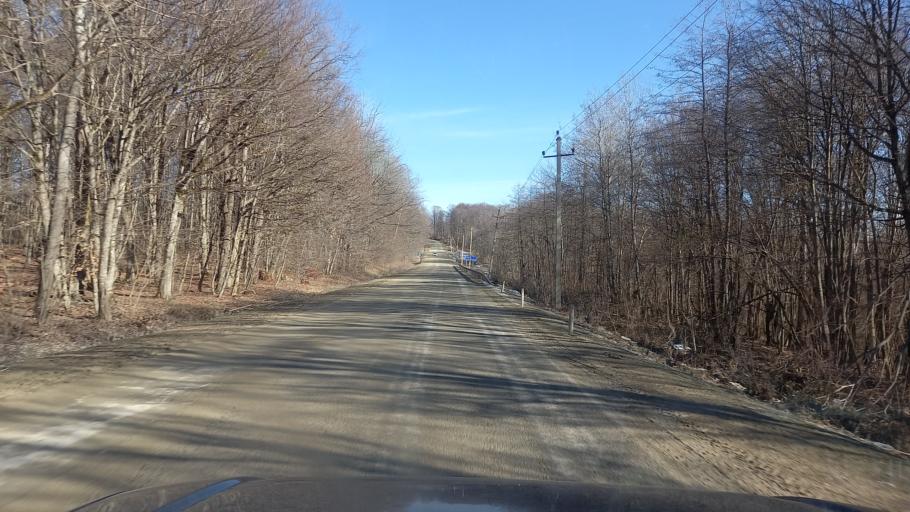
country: RU
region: Adygeya
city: Kamennomostskiy
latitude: 44.2784
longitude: 40.2867
